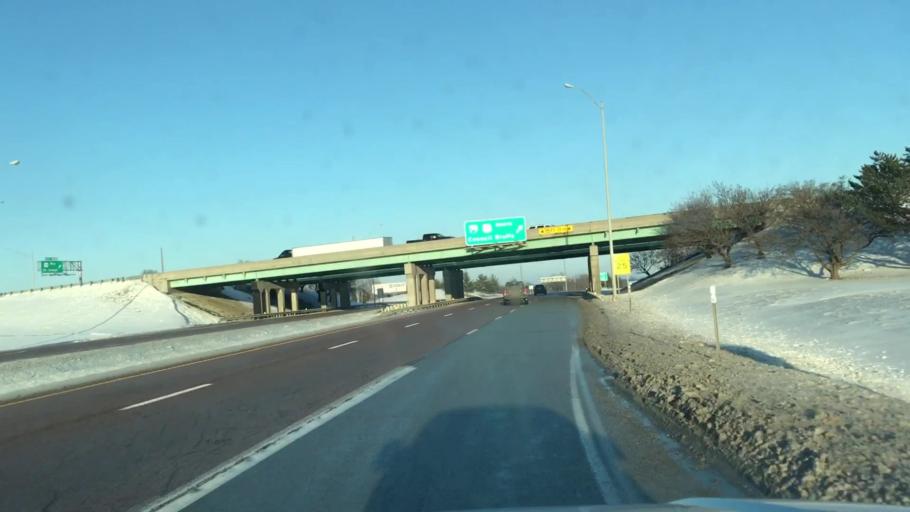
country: US
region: Missouri
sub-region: Buchanan County
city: Saint Joseph
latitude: 39.7489
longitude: -94.7907
